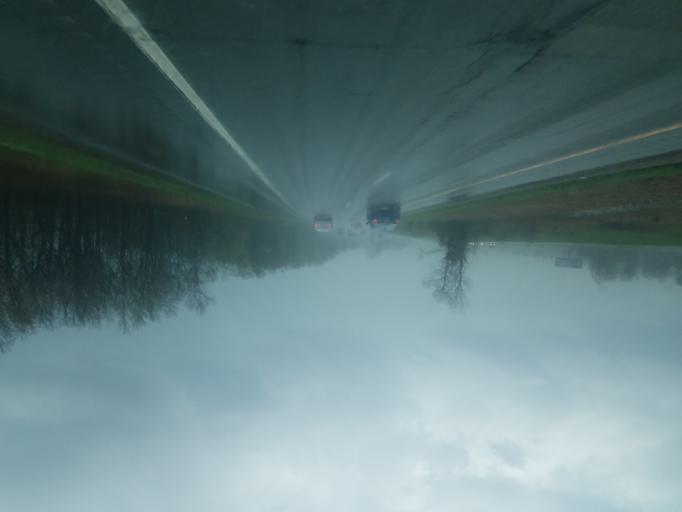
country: US
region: Michigan
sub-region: Livingston County
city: Fowlerville
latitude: 42.6464
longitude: -84.1007
